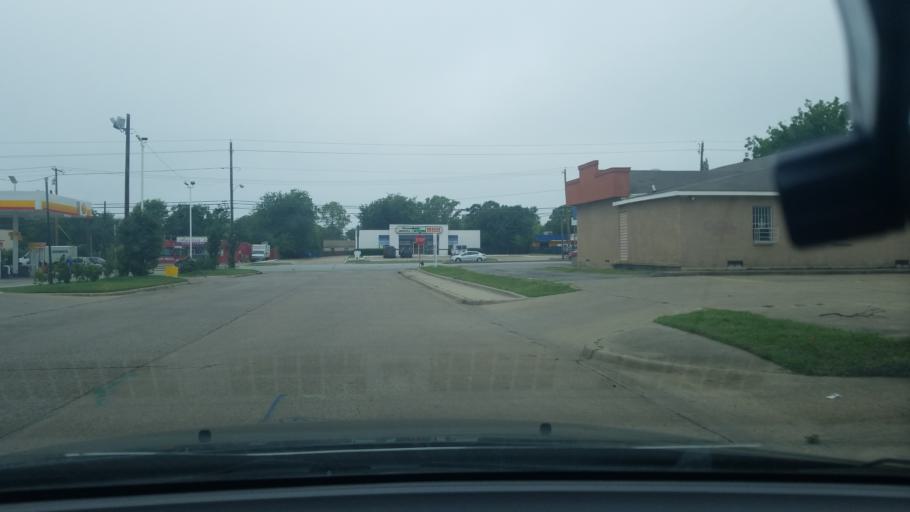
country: US
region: Texas
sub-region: Dallas County
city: Balch Springs
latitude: 32.7550
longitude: -96.6819
